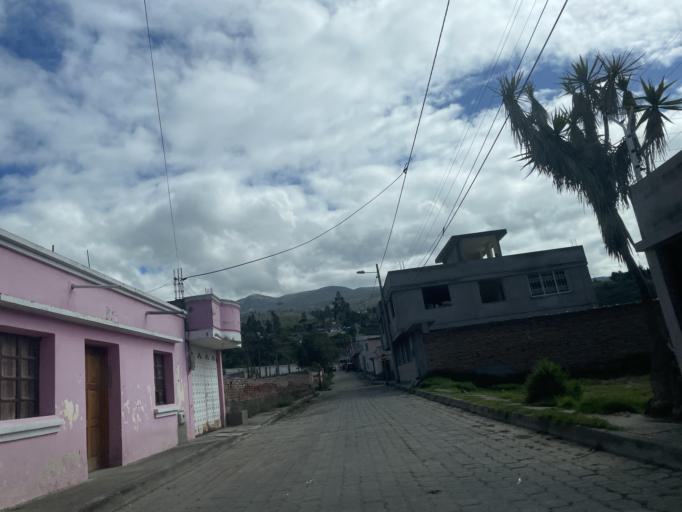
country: EC
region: Chimborazo
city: Guano
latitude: -1.6084
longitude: -78.6326
